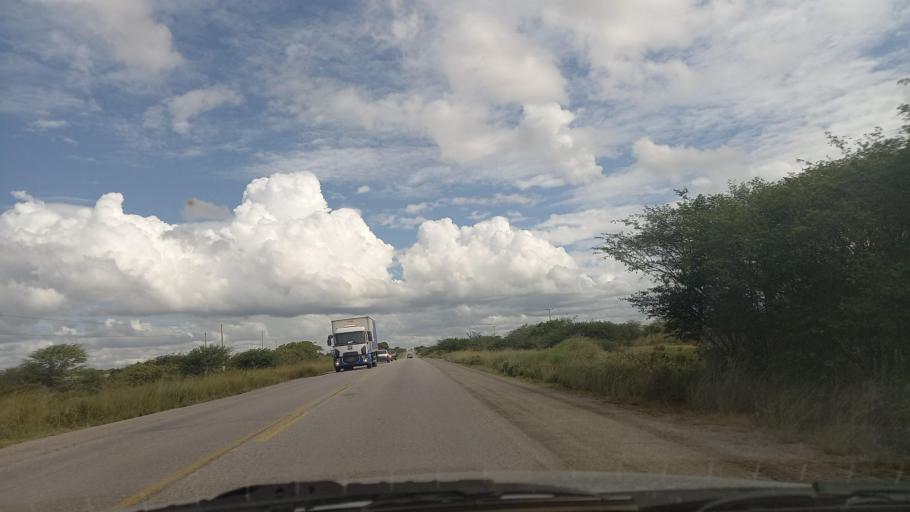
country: BR
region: Pernambuco
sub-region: Cachoeirinha
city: Cachoeirinha
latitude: -8.4347
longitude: -36.2021
